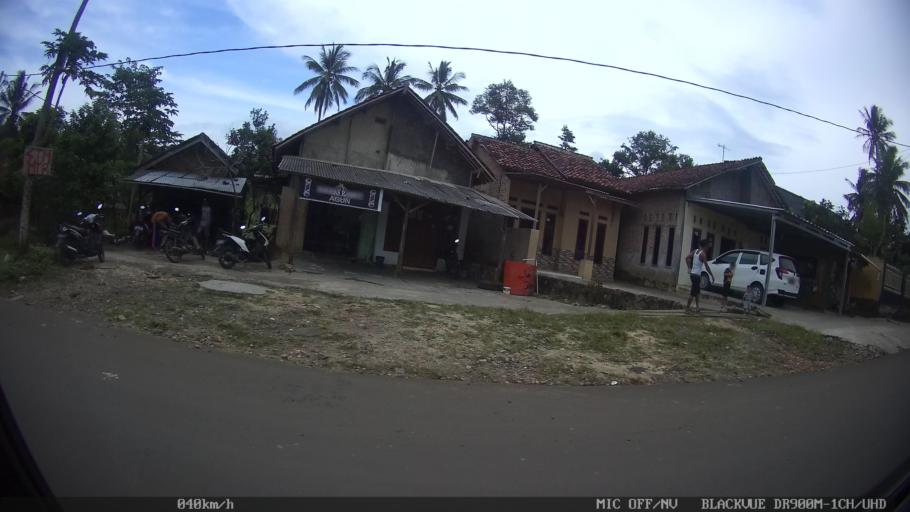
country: ID
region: Lampung
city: Bandarlampung
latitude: -5.4255
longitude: 105.1954
